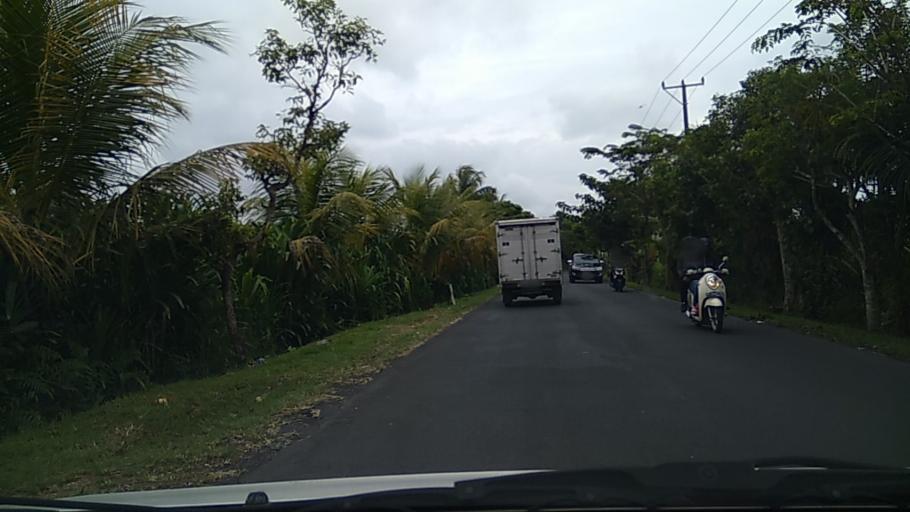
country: ID
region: Bali
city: Banjar Kembangsari
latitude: -8.5003
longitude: 115.2101
